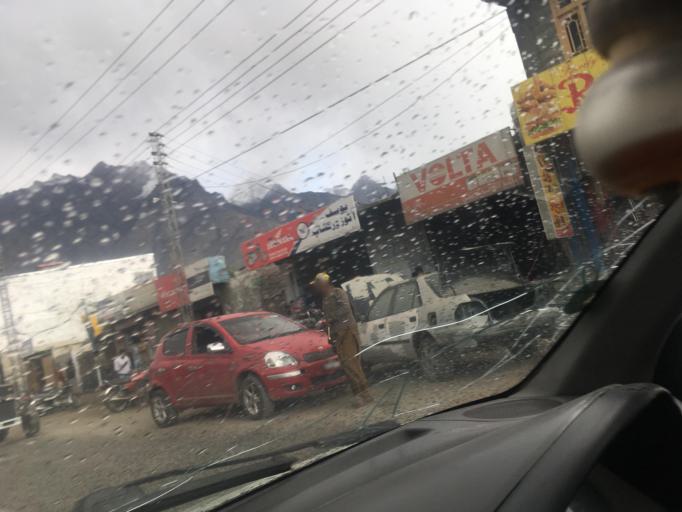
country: PK
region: Gilgit-Baltistan
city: Skardu
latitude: 35.3022
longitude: 75.6254
